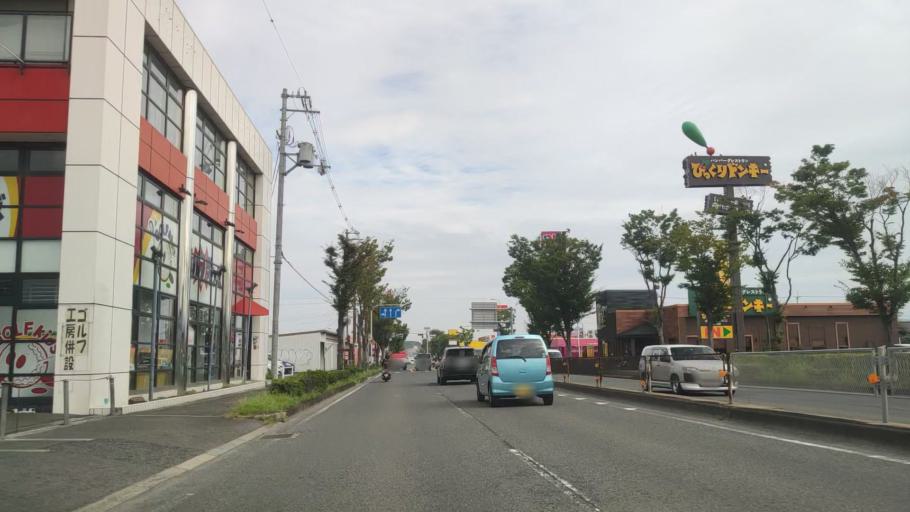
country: JP
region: Osaka
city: Tondabayashicho
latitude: 34.5364
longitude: 135.6047
